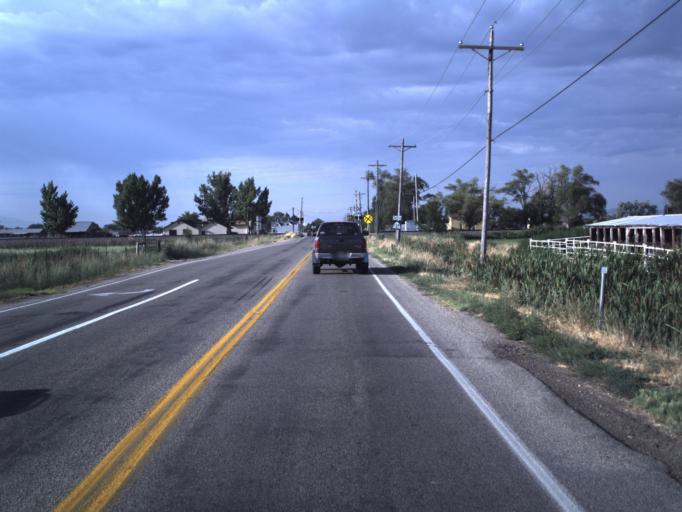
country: US
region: Utah
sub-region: Weber County
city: Plain City
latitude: 41.2457
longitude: -112.0926
